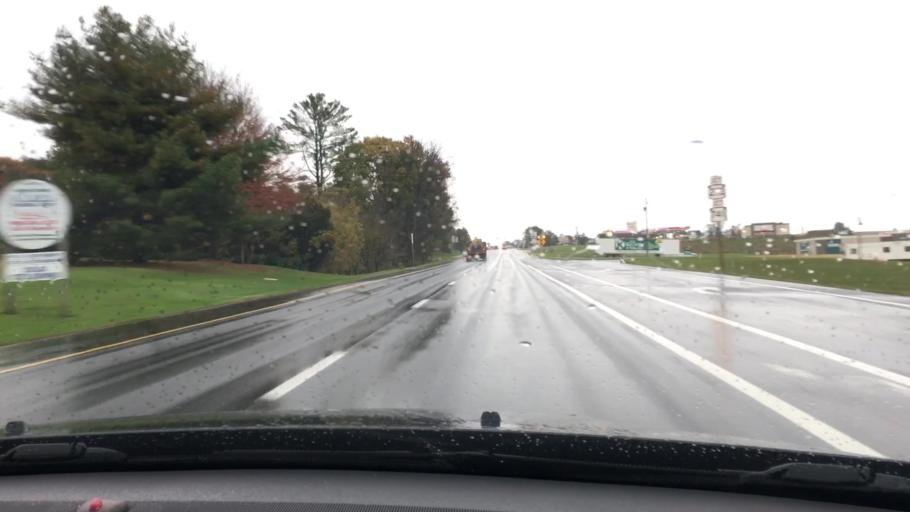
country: US
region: Pennsylvania
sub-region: Lancaster County
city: Willow Street
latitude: 39.9896
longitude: -76.2849
